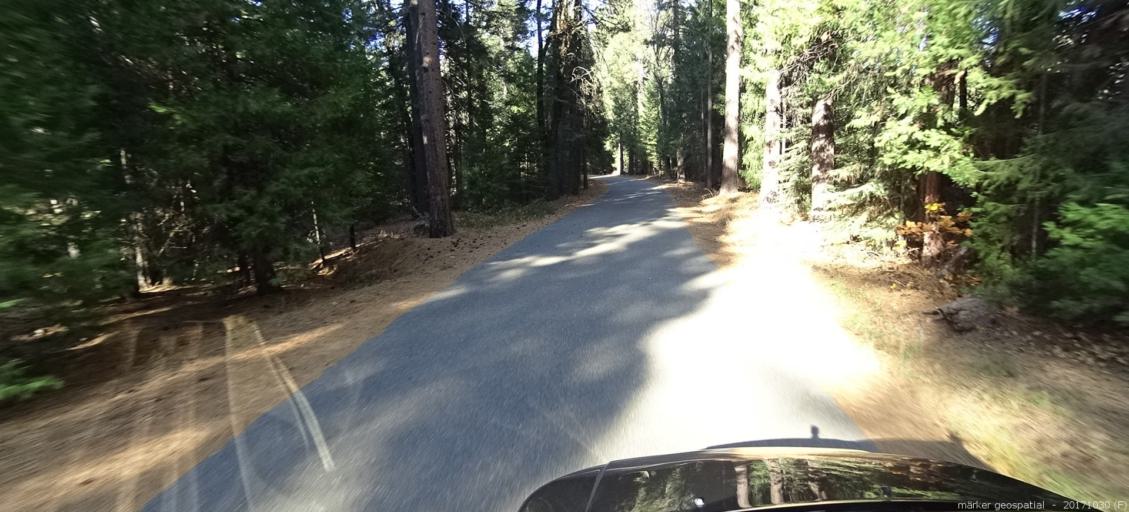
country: US
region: California
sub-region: Shasta County
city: Shingletown
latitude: 40.5257
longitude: -121.6890
